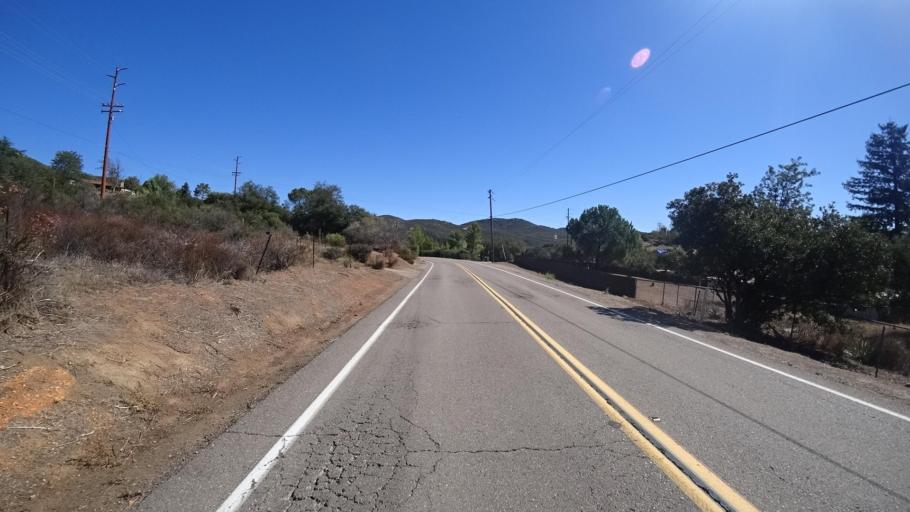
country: US
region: California
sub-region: San Diego County
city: Descanso
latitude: 32.8024
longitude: -116.6436
